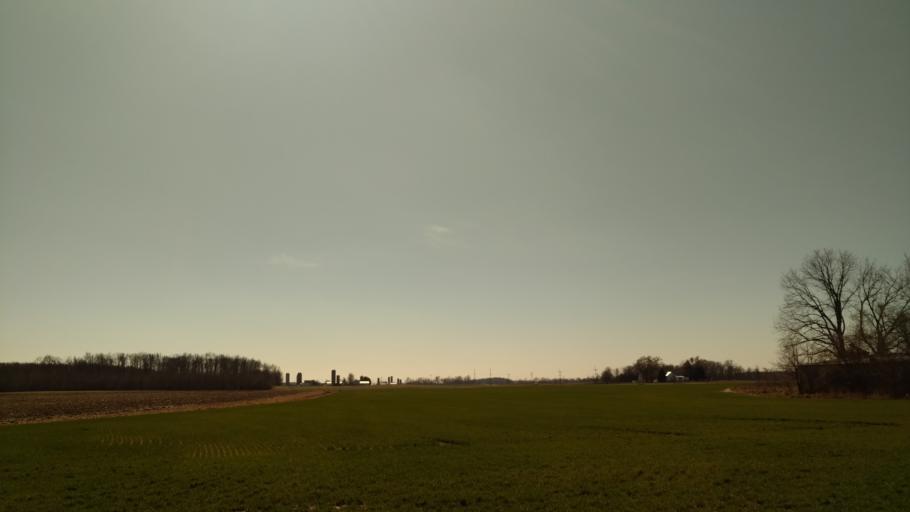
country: US
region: Ohio
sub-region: Marion County
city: Prospect
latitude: 40.4946
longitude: -83.1491
